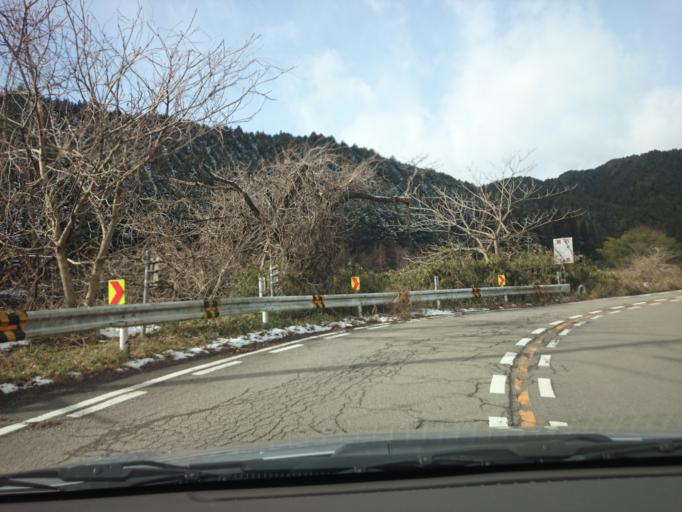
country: JP
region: Gifu
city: Gujo
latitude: 35.7384
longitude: 137.0650
